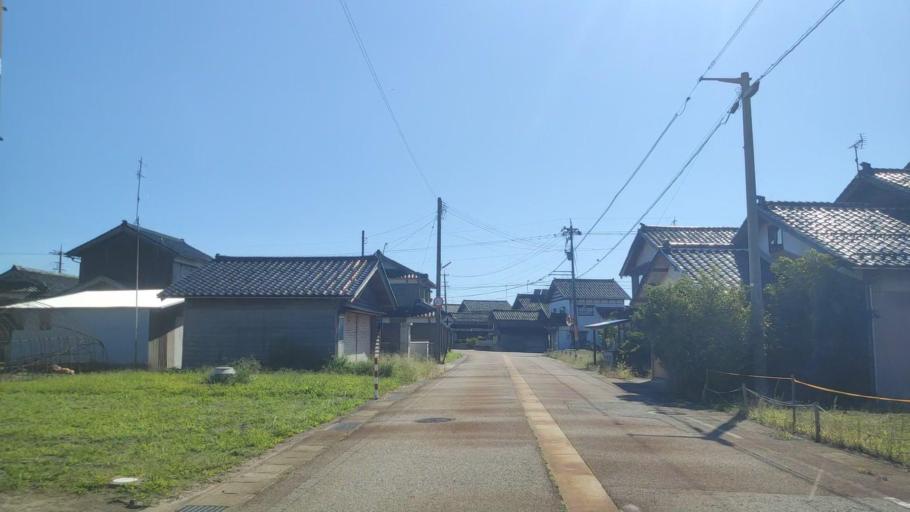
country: JP
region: Ishikawa
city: Nanao
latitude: 37.4480
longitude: 137.2896
